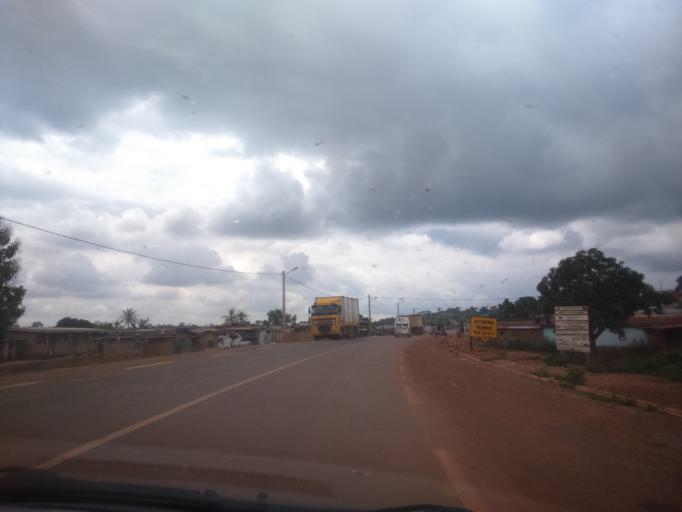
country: CI
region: Moyen-Comoe
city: Abengourou
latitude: 6.6391
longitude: -3.7139
